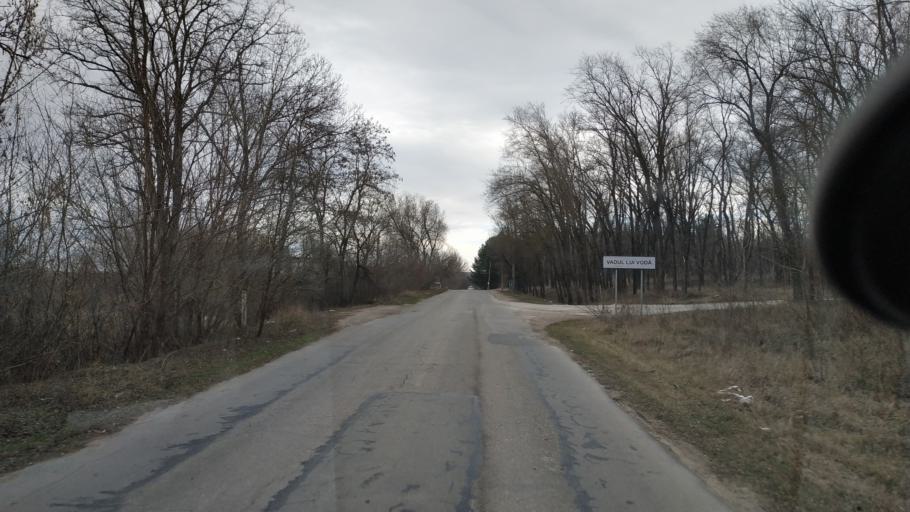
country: MD
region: Chisinau
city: Vadul lui Voda
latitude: 47.1041
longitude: 29.0656
